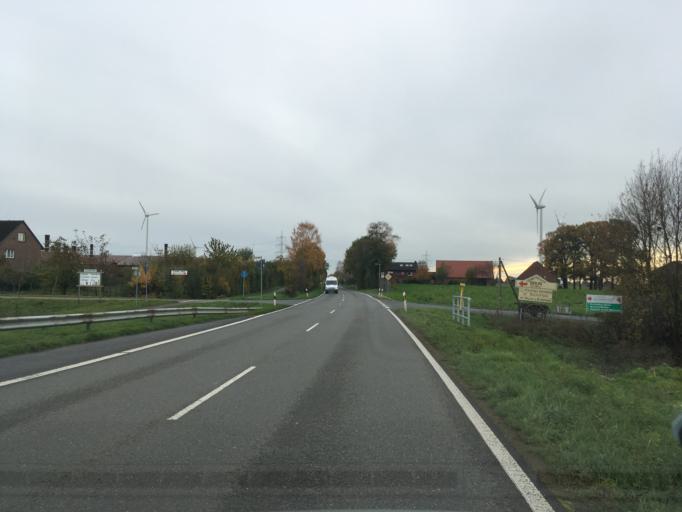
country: DE
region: North Rhine-Westphalia
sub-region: Regierungsbezirk Munster
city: Heiden
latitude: 51.8135
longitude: 6.9468
